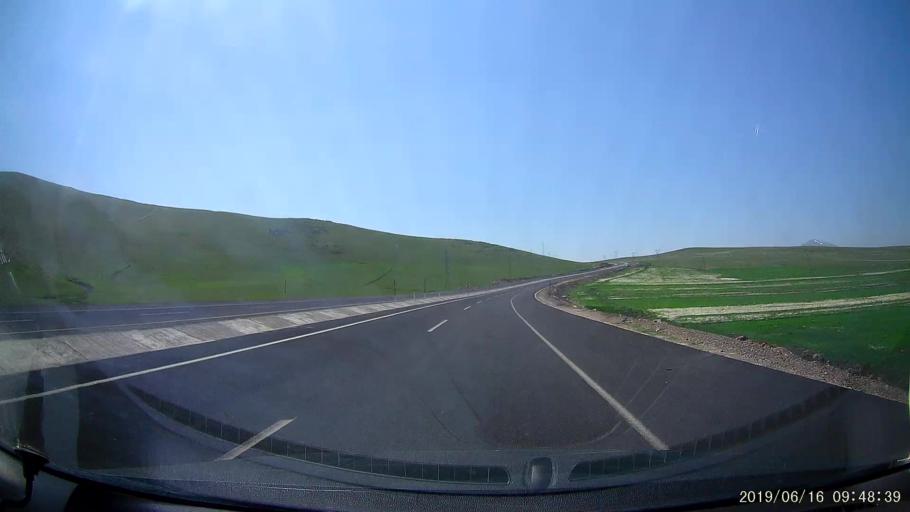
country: TR
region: Kars
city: Digor
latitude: 40.4312
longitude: 43.3547
